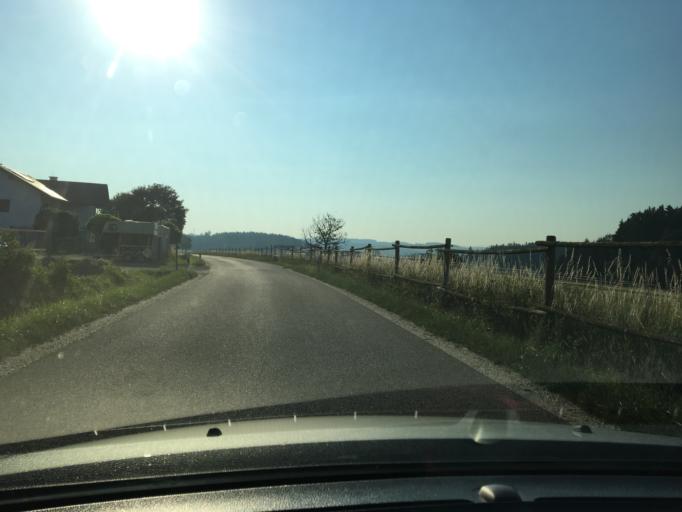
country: DE
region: Bavaria
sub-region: Lower Bavaria
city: Vilsbiburg
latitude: 48.4396
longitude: 12.3157
